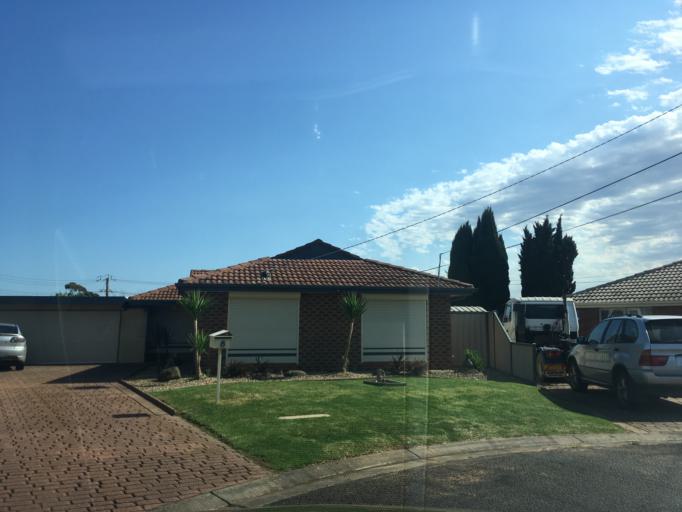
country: AU
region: Victoria
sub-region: Wyndham
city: Hoppers Crossing
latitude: -37.8708
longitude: 144.7047
